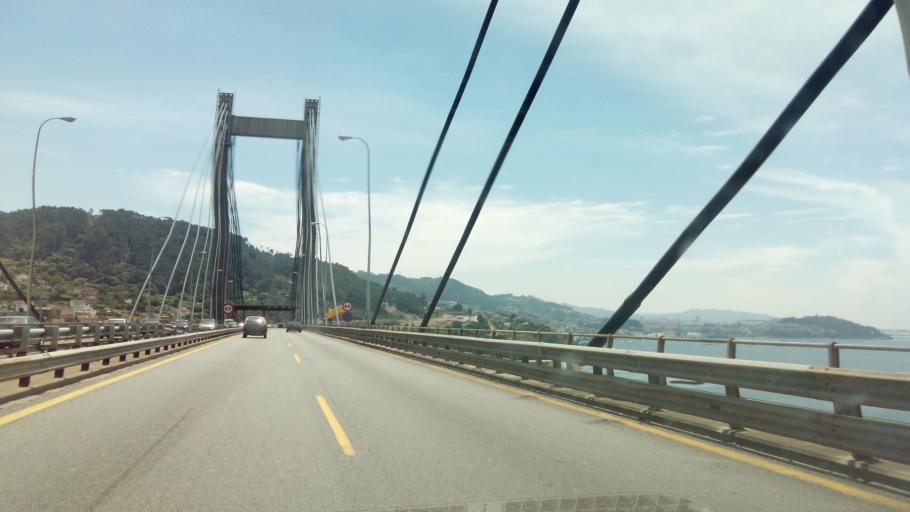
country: ES
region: Galicia
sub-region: Provincia de Pontevedra
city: Redondela
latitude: 42.2890
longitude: -8.6604
